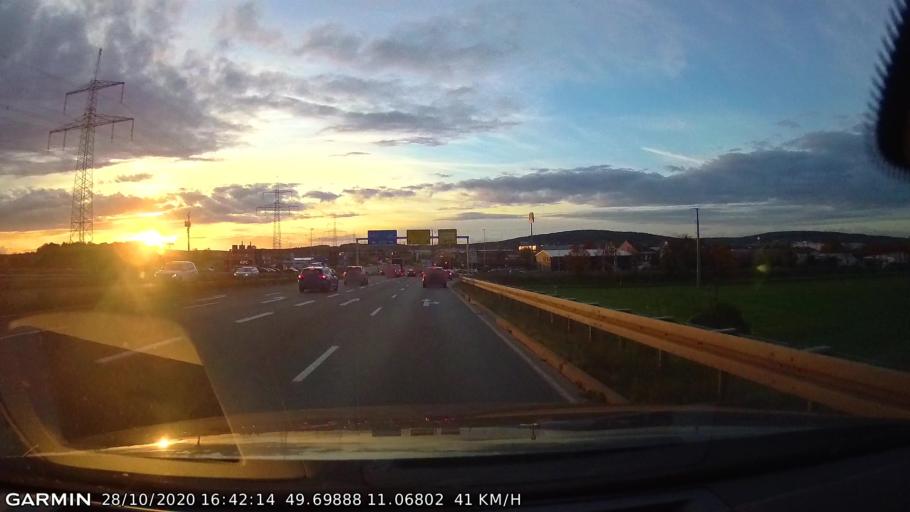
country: DE
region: Bavaria
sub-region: Upper Franconia
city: Forchheim
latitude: 49.6989
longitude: 11.0678
